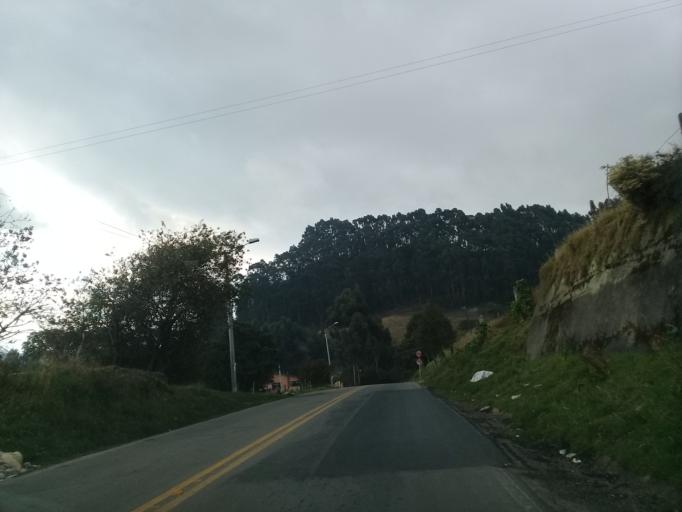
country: CO
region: Cundinamarca
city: Zipaquira
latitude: 5.0454
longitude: -74.0498
